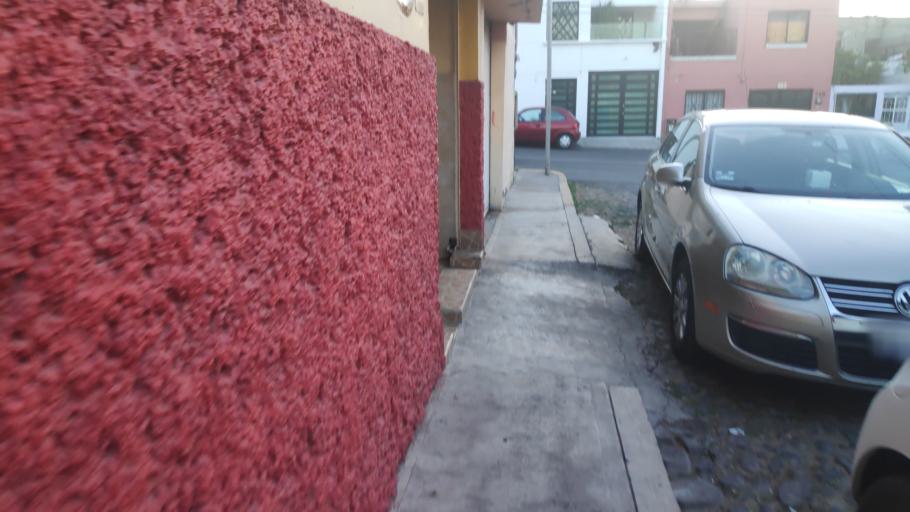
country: MX
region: Queretaro
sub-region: Queretaro
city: Santiago de Queretaro
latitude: 20.5809
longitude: -100.3716
